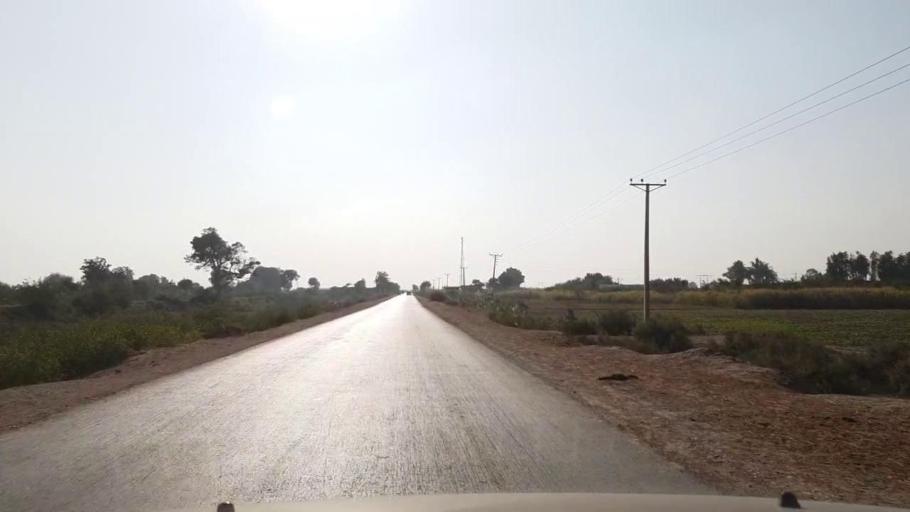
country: PK
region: Sindh
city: Tando Muhammad Khan
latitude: 25.0549
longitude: 68.4548
